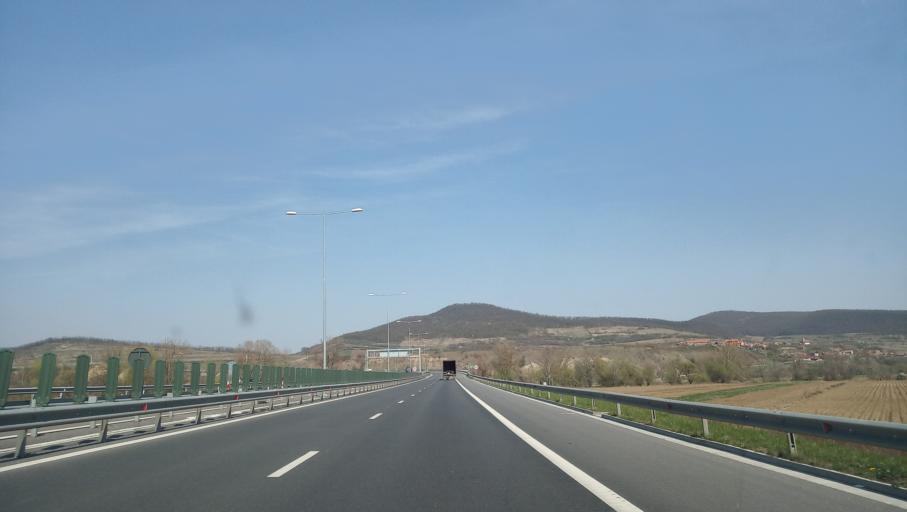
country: RO
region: Alba
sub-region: Municipiul Aiud
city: Aiud
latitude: 46.3342
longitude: 23.7306
